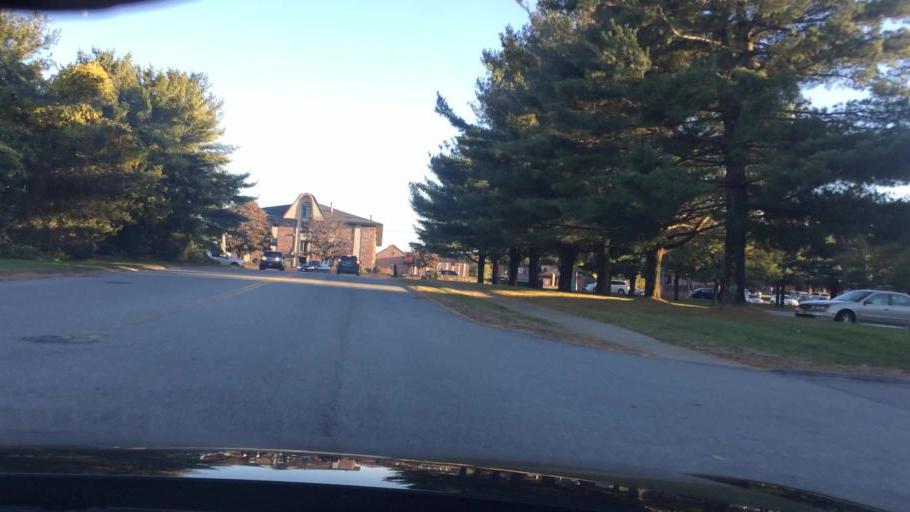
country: US
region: Massachusetts
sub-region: Middlesex County
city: Chelmsford
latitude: 42.6274
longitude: -71.3591
